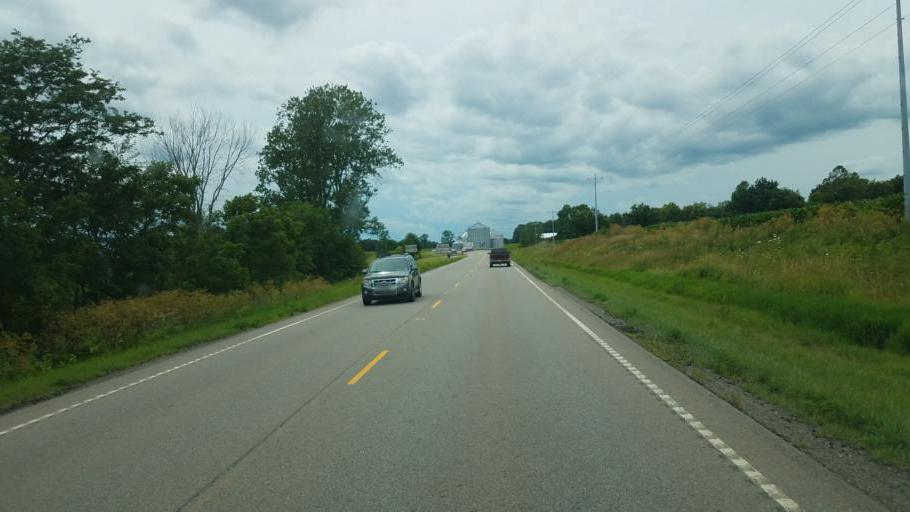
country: US
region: Ohio
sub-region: Licking County
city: Utica
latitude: 40.2315
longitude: -82.4924
